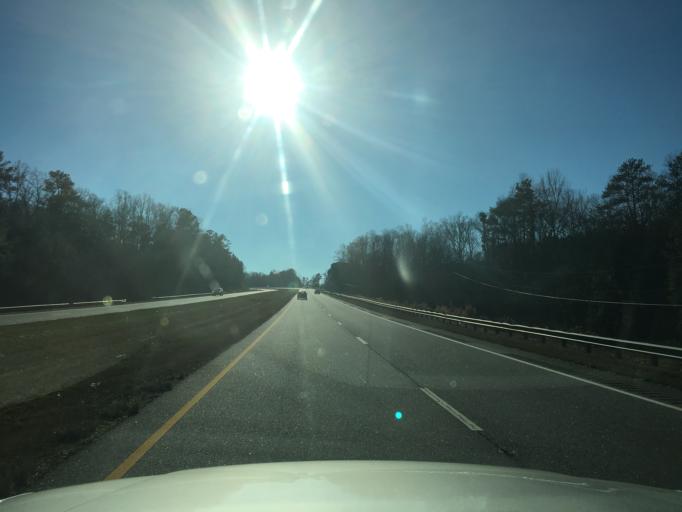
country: US
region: Georgia
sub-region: Carroll County
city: Carrollton
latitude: 33.4679
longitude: -85.1189
